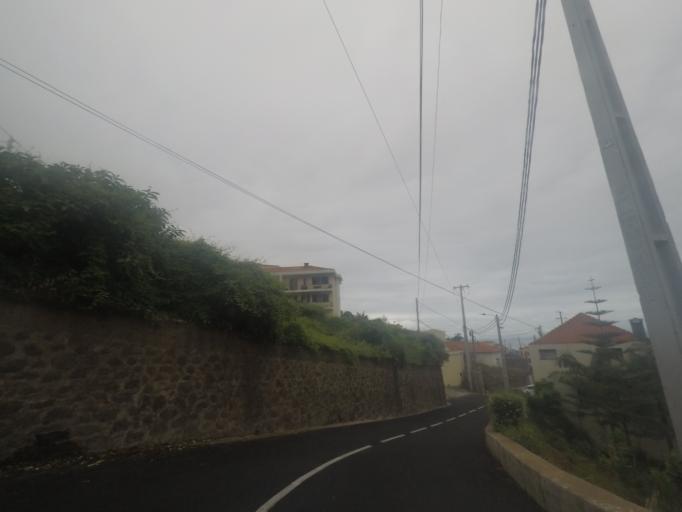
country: PT
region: Madeira
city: Camara de Lobos
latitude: 32.6654
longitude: -16.9713
